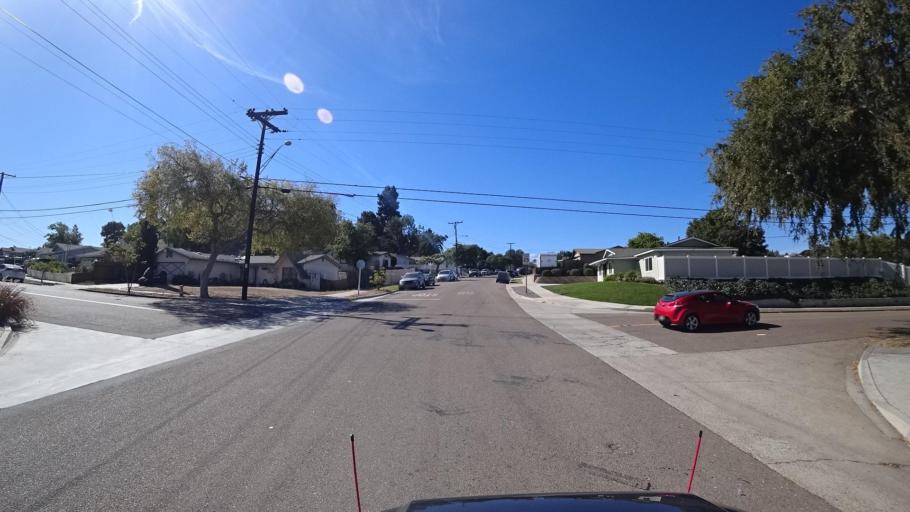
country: US
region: California
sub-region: San Diego County
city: Lemon Grove
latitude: 32.7221
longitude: -117.0205
